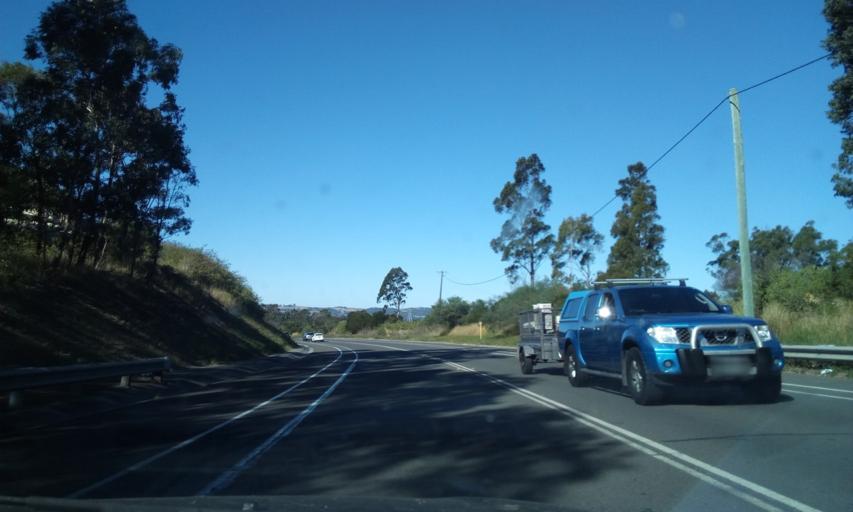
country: AU
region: New South Wales
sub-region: Wollongong
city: Dapto
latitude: -34.5183
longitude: 150.7838
